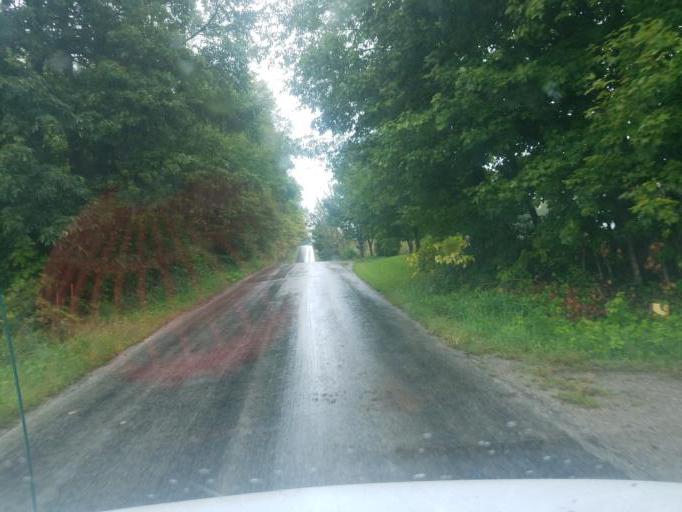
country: US
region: Ohio
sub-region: Wayne County
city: West Salem
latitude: 40.9377
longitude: -82.0434
